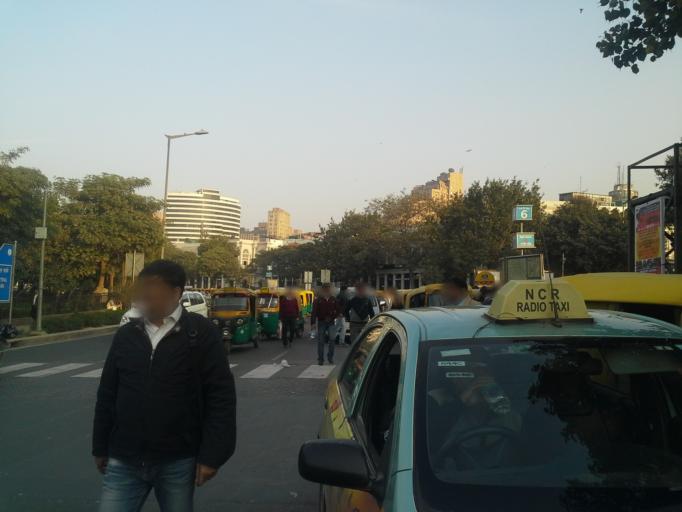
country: IN
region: NCT
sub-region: New Delhi
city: New Delhi
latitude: 28.6318
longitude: 77.2191
